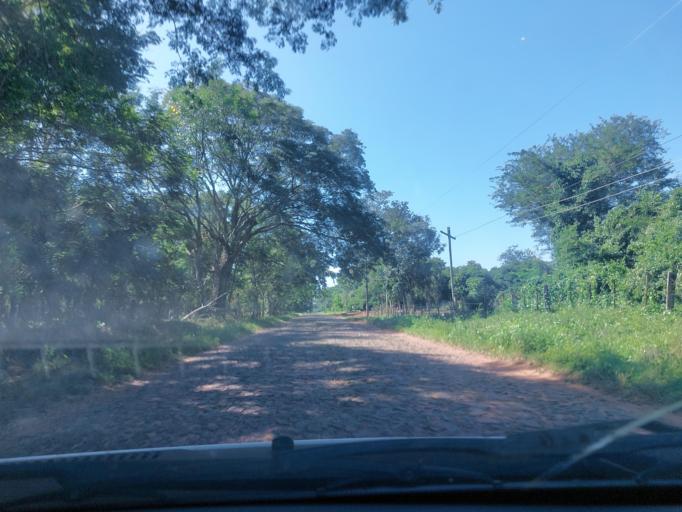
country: PY
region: San Pedro
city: Itacurubi del Rosario
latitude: -24.5730
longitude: -56.5977
